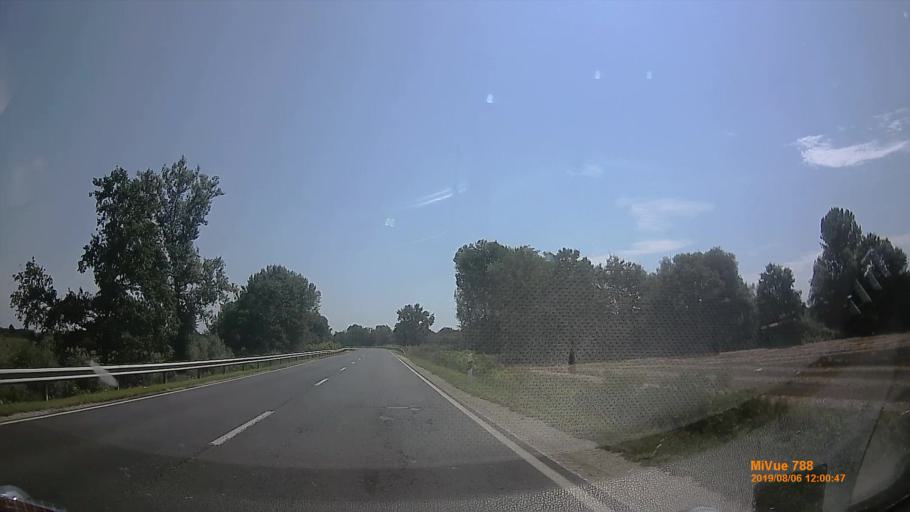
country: HU
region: Vas
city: Vasvar
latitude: 47.0601
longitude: 16.7531
